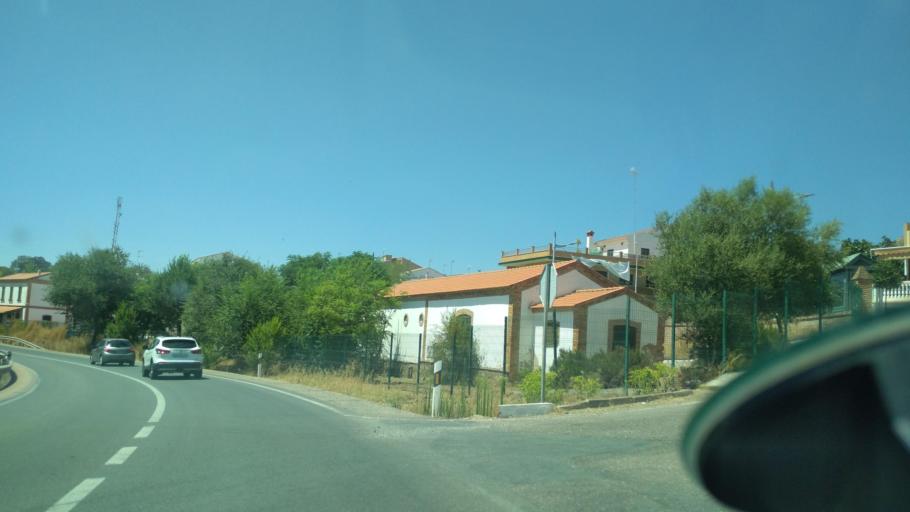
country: ES
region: Andalusia
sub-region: Provincia de Huelva
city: Zalamea la Real
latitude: 37.6918
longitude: -6.6304
